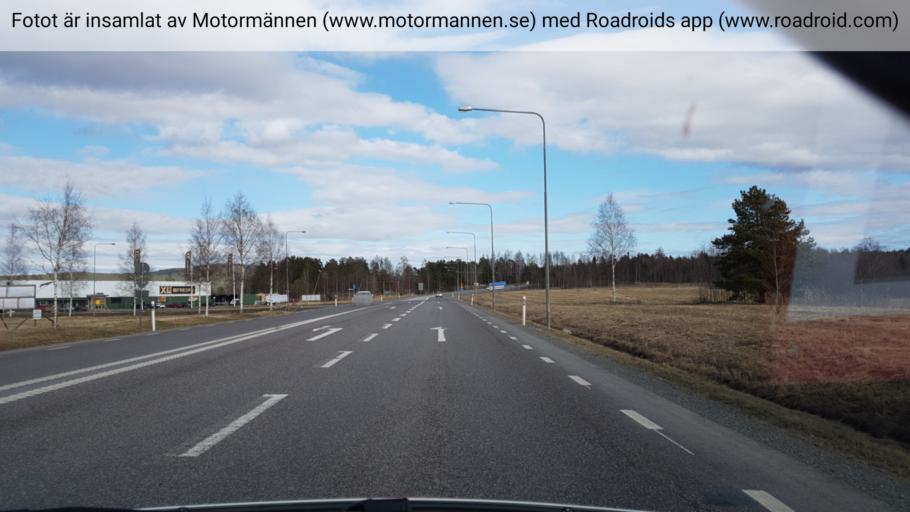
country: SE
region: Vaesternorrland
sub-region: Solleftea Kommun
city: Solleftea
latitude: 63.1594
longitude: 17.3042
